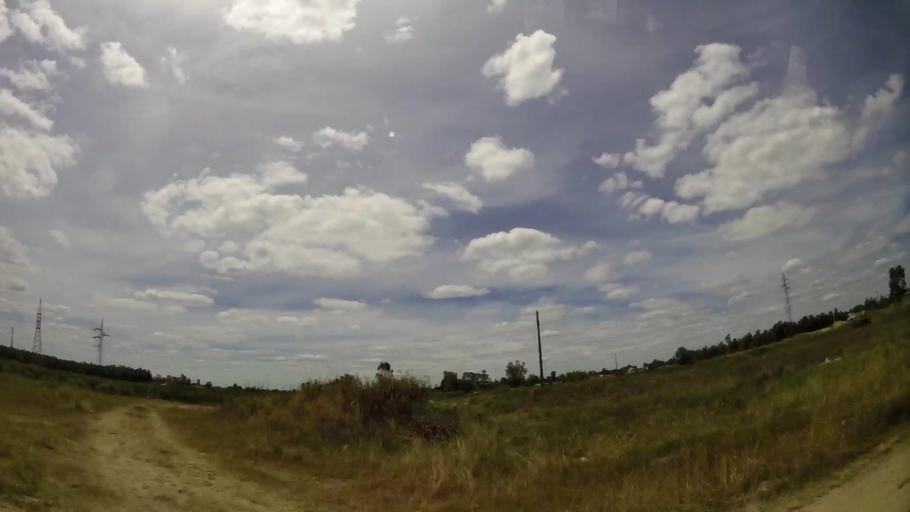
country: UY
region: San Jose
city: Delta del Tigre
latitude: -34.7705
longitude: -56.3757
